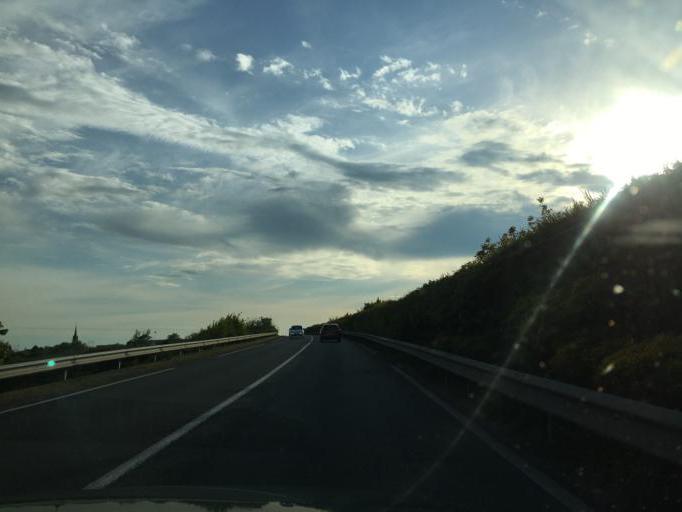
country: FR
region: Centre
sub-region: Departement du Loiret
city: Ormes
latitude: 47.9466
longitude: 1.8234
